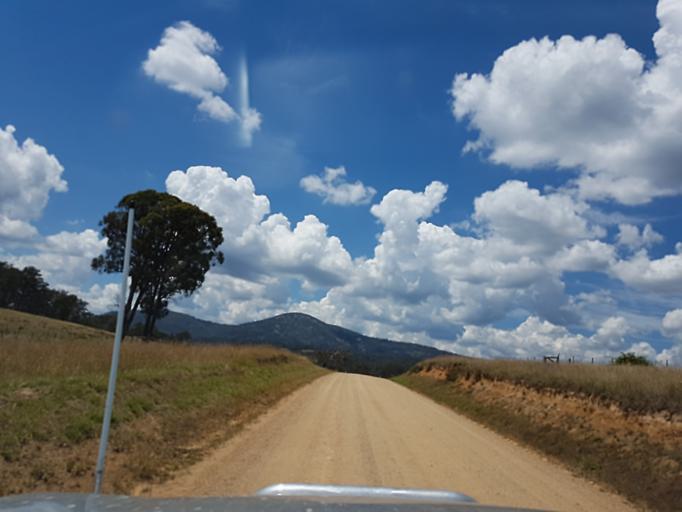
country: AU
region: Victoria
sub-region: Alpine
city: Mount Beauty
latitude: -36.8998
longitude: 147.8514
